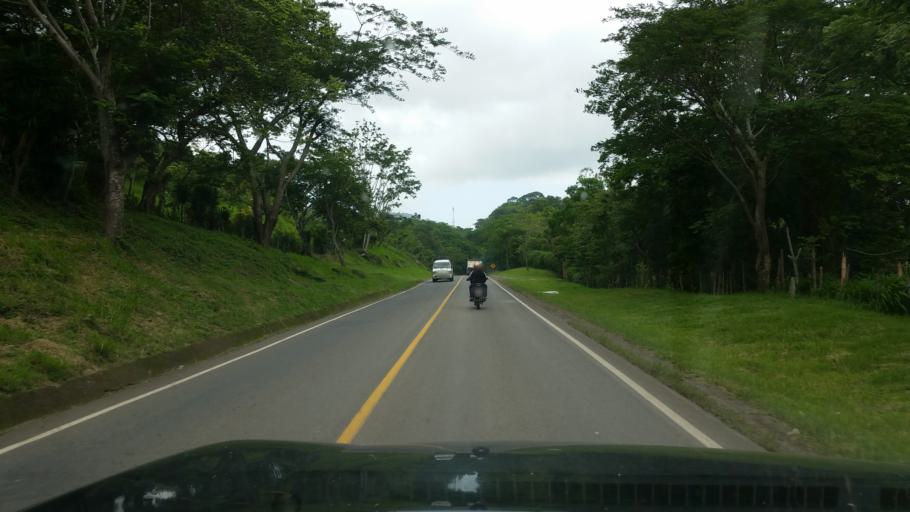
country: NI
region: Matagalpa
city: Matagalpa
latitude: 12.9405
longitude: -85.8870
